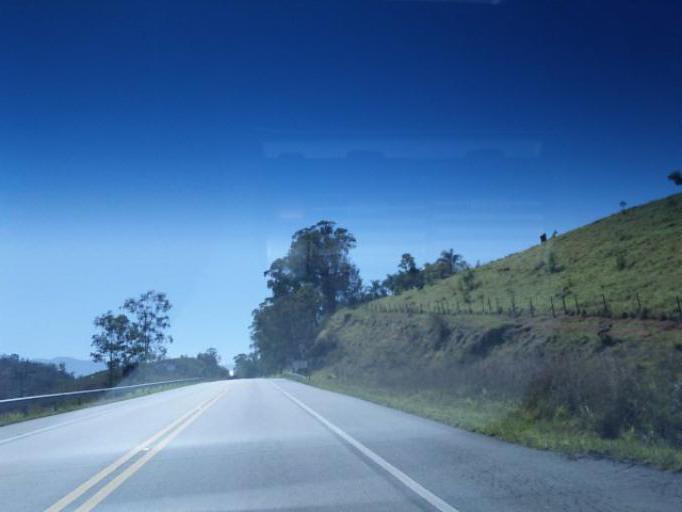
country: BR
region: Sao Paulo
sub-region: Tremembe
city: Tremembe
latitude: -22.9201
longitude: -45.5934
